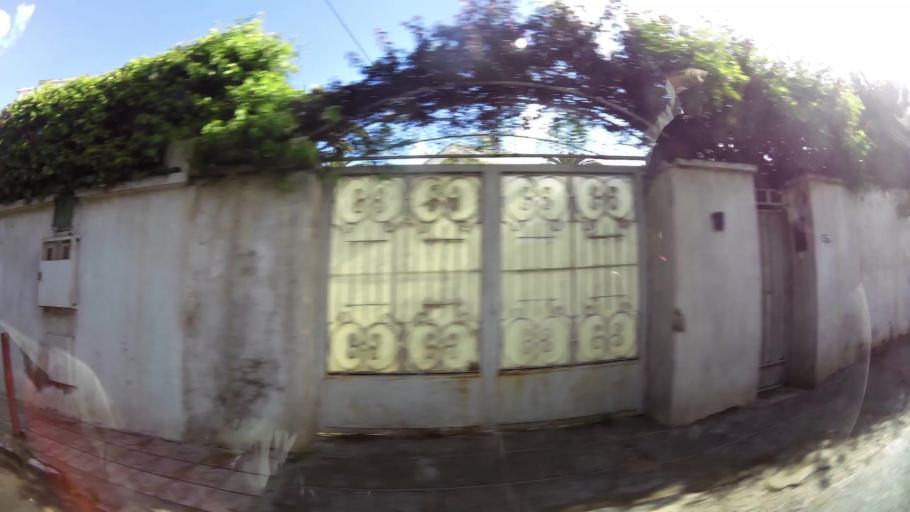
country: MA
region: Grand Casablanca
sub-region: Casablanca
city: Casablanca
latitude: 33.5809
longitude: -7.6271
